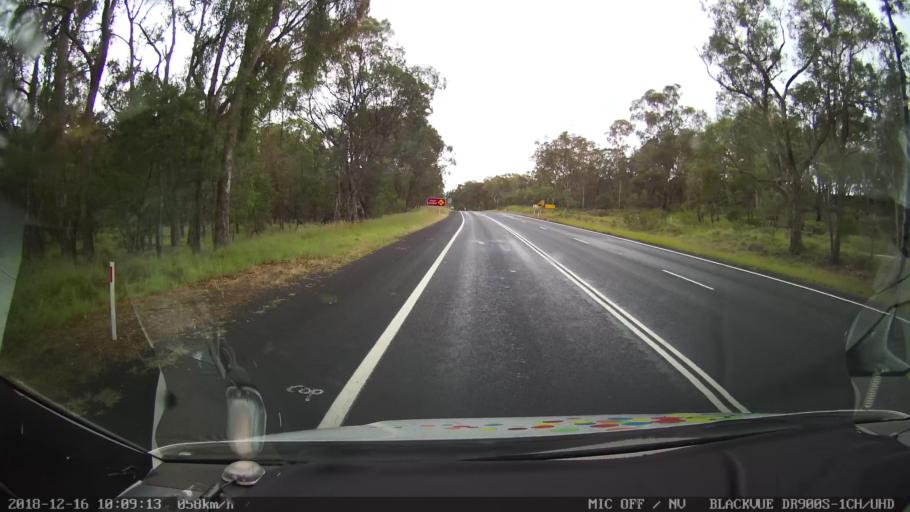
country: AU
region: New South Wales
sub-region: Glen Innes Severn
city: Glen Innes
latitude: -29.3252
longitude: 151.9148
